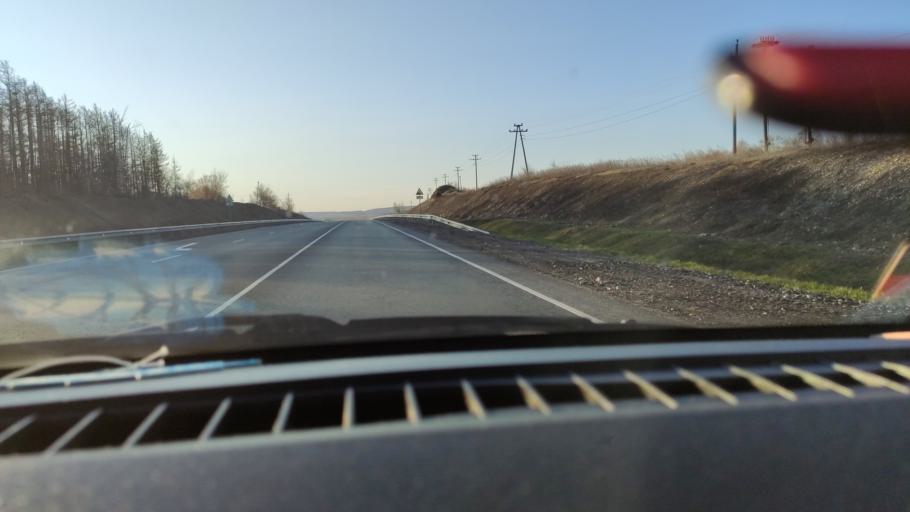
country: RU
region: Saratov
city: Shikhany
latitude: 52.1445
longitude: 47.2004
